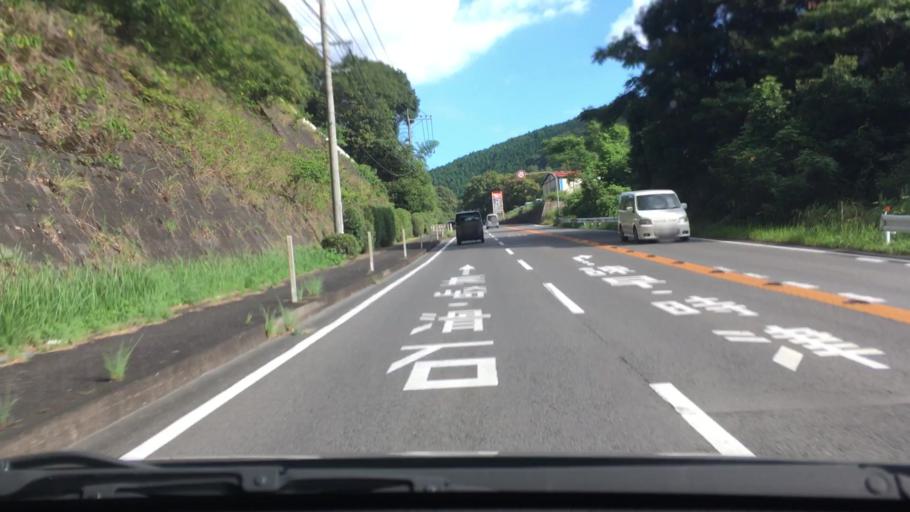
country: JP
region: Nagasaki
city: Togitsu
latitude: 32.8213
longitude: 129.8001
